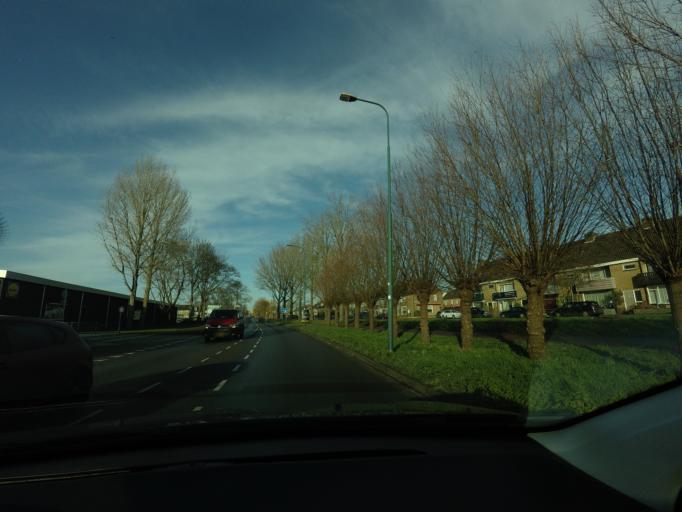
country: NL
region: Utrecht
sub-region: Gemeente Woerden
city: Woerden
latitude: 52.0812
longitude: 4.8775
